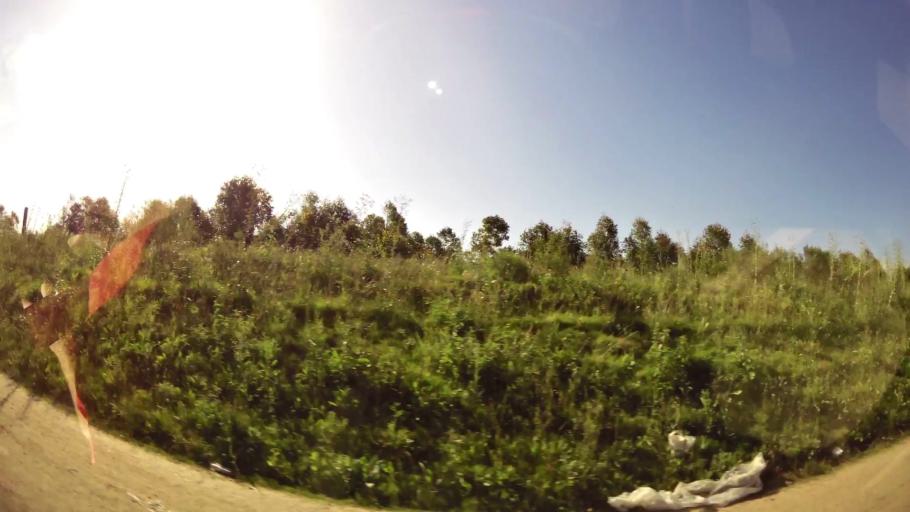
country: UY
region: Canelones
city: La Paz
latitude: -34.8111
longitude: -56.1667
